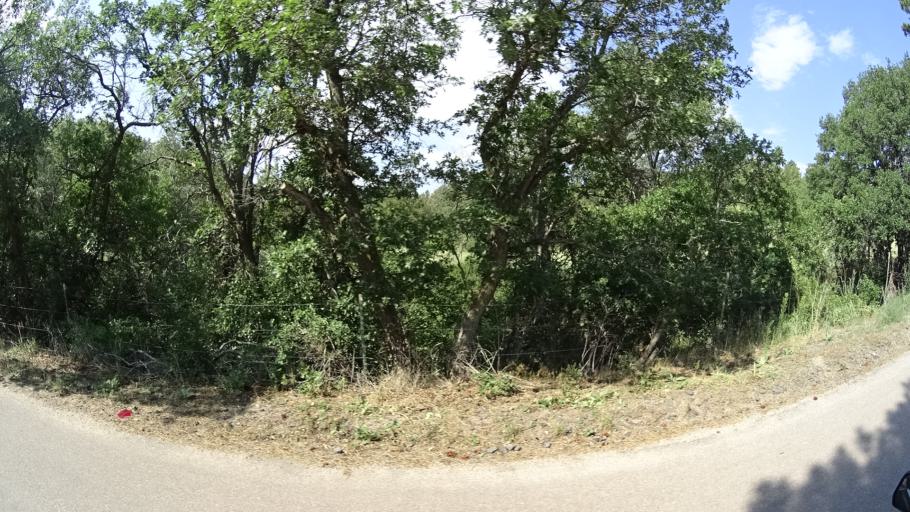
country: US
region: Colorado
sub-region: El Paso County
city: Fort Carson
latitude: 38.7197
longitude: -104.8248
